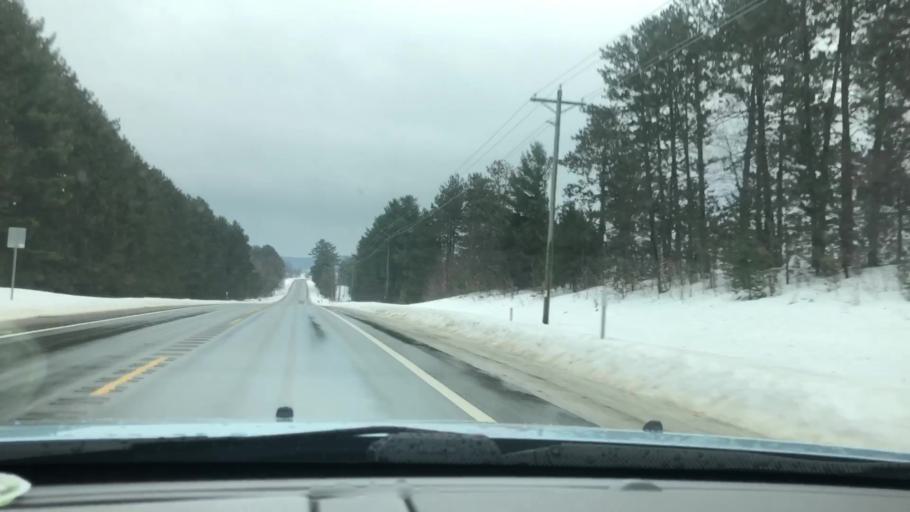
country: US
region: Michigan
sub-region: Charlevoix County
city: Boyne City
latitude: 45.0945
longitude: -84.9665
